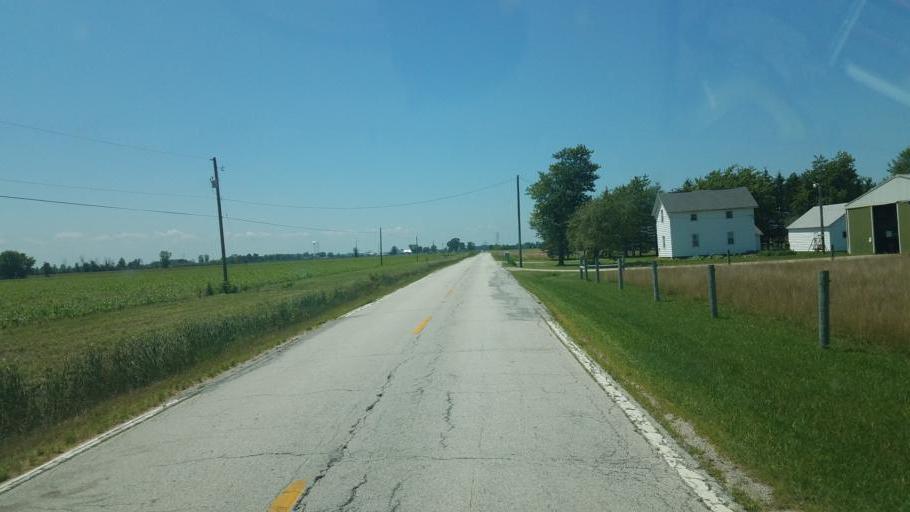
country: US
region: Ohio
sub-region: Ottawa County
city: Oak Harbor
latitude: 41.4429
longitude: -83.1160
